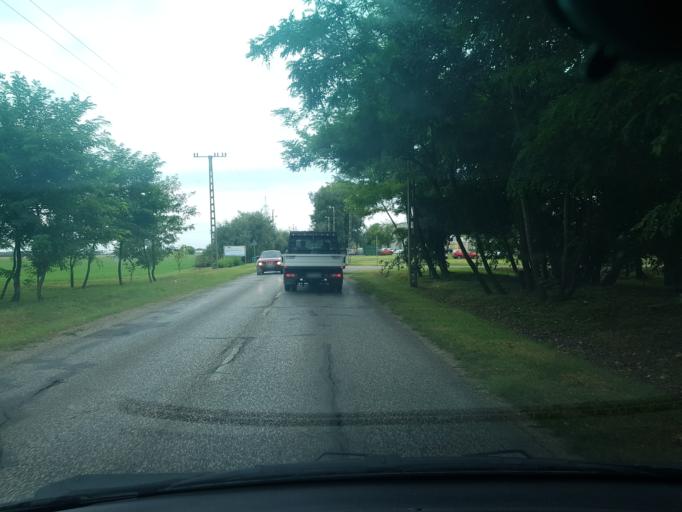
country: HU
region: Pest
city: Taksony
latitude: 47.3274
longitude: 19.0574
